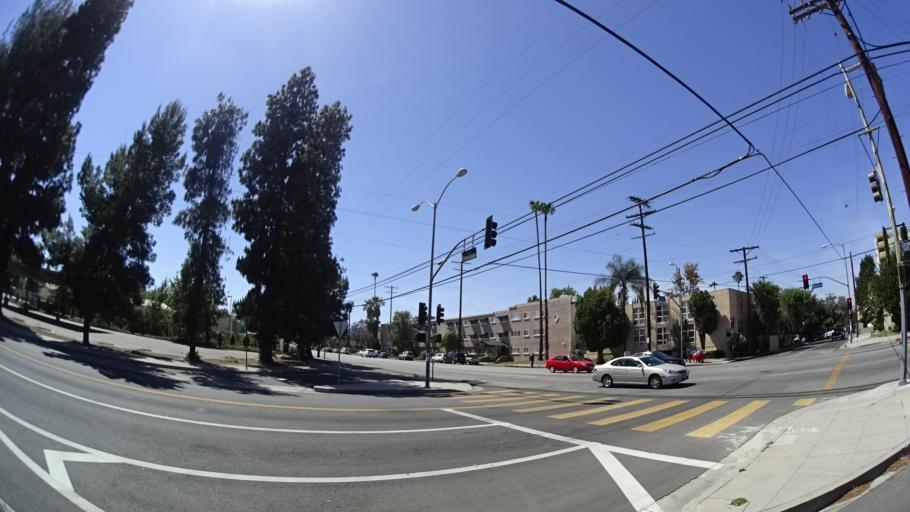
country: US
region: California
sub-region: Los Angeles County
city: Van Nuys
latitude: 34.1791
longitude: -118.4181
